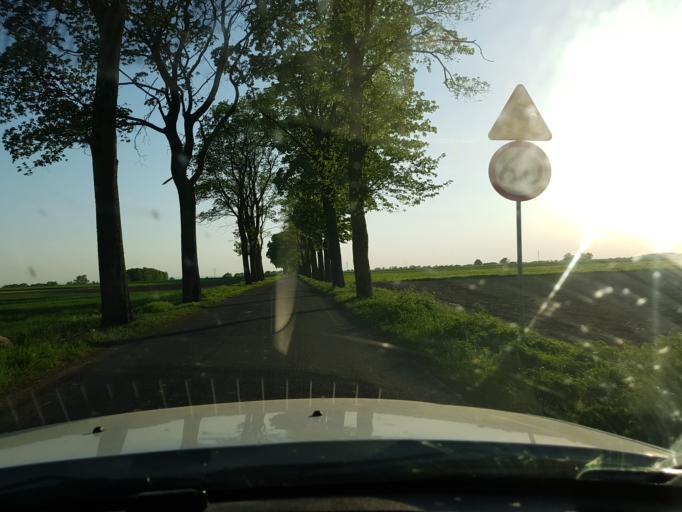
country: PL
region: West Pomeranian Voivodeship
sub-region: Powiat goleniowski
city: Mosty
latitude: 53.4736
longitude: 14.9585
